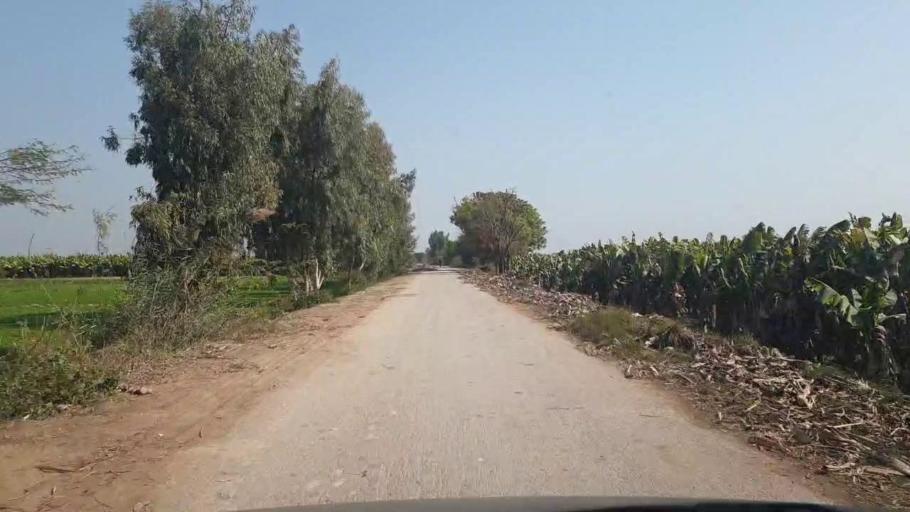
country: PK
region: Sindh
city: Tando Adam
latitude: 25.8202
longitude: 68.6464
